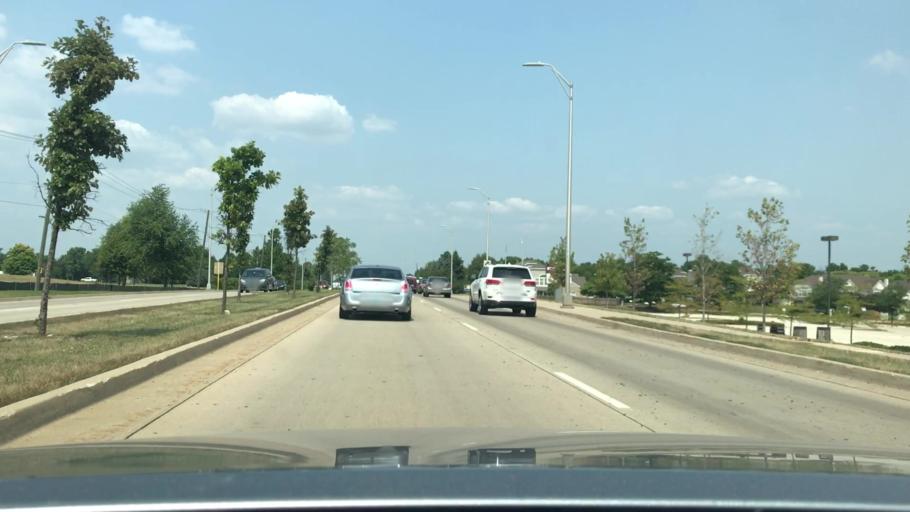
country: US
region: Illinois
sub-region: Will County
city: Crystal Lawns
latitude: 41.5671
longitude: -88.2004
